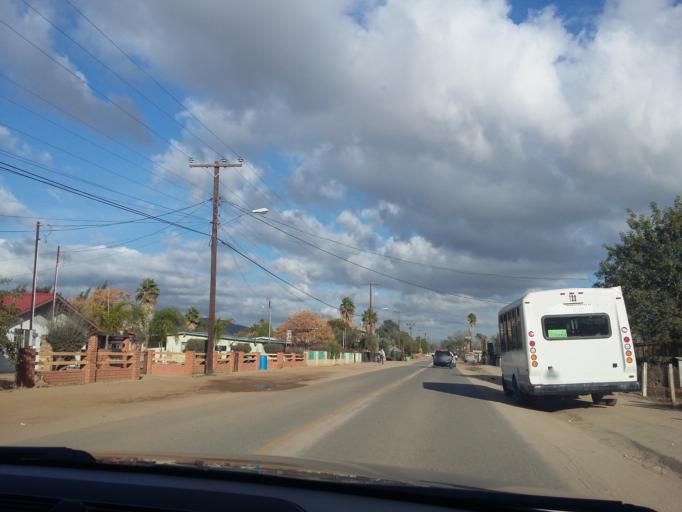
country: MX
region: Baja California
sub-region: Ensenada
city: Rancho Verde
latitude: 32.0735
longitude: -116.6302
